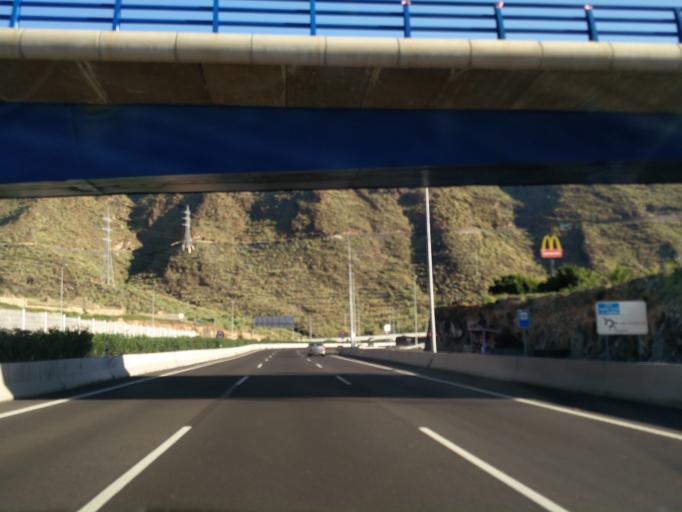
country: ES
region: Canary Islands
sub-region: Provincia de Santa Cruz de Tenerife
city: Candelaria
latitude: 28.3813
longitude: -16.3633
